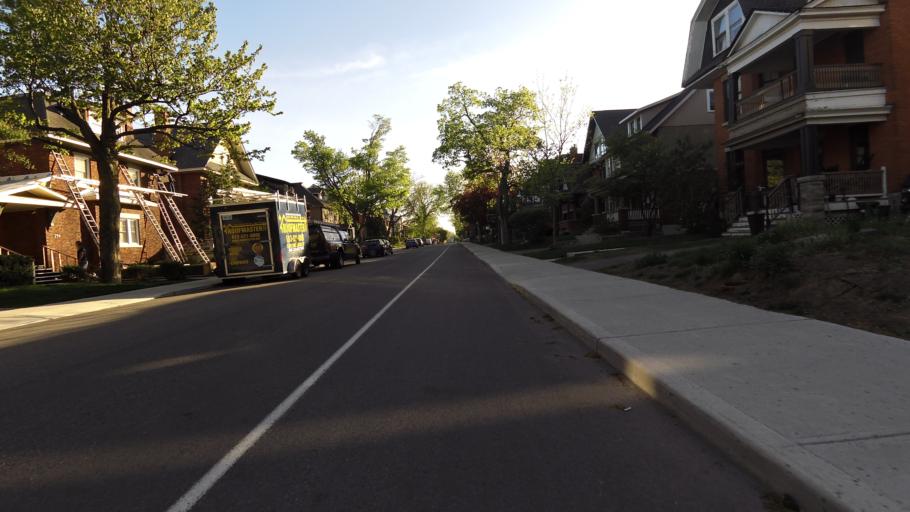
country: CA
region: Ontario
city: Ottawa
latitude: 45.4029
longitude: -75.6929
